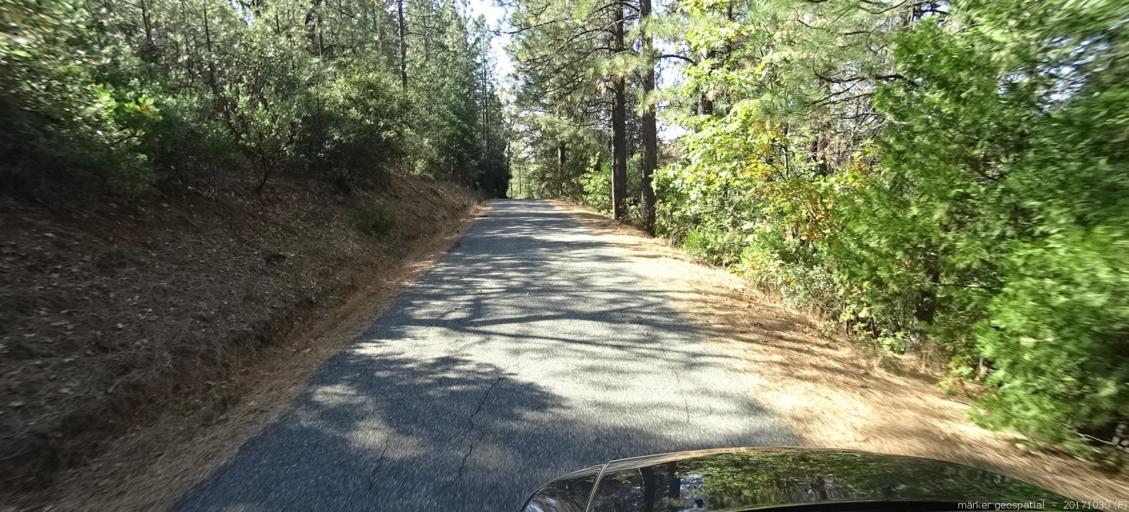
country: US
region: California
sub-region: Shasta County
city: Shingletown
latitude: 40.5809
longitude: -121.8748
